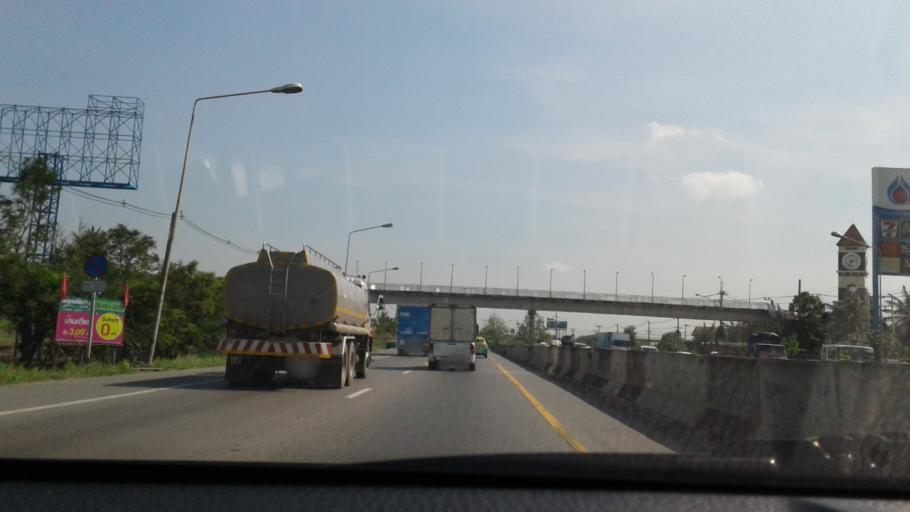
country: TH
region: Nonthaburi
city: Pak Kret
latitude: 13.9555
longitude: 100.4869
